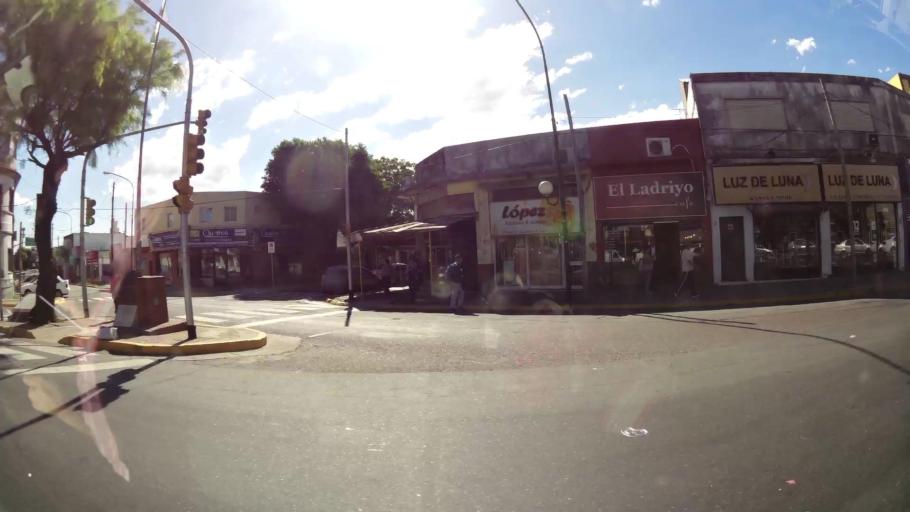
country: AR
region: Buenos Aires
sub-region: Partido de San Isidro
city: San Isidro
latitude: -34.5116
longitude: -58.5672
